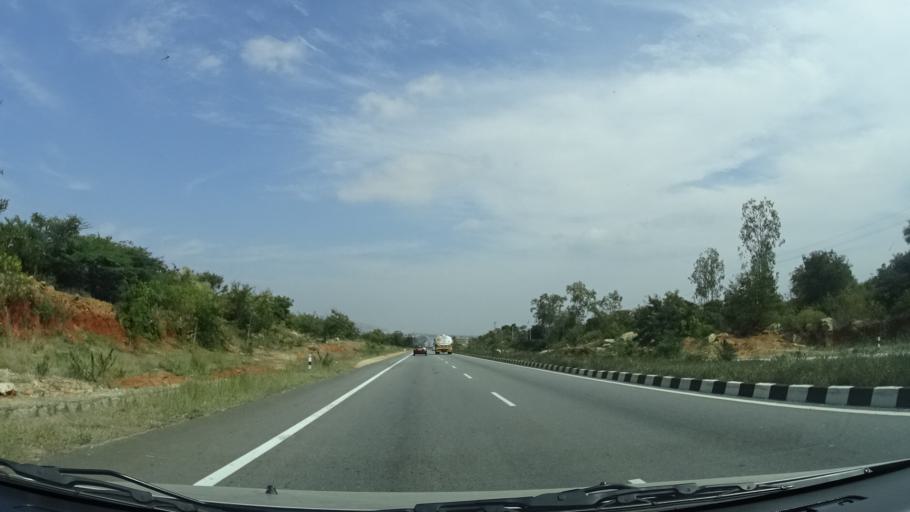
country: IN
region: Karnataka
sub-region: Chikkaballapur
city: Chik Ballapur
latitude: 13.5562
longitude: 77.7777
